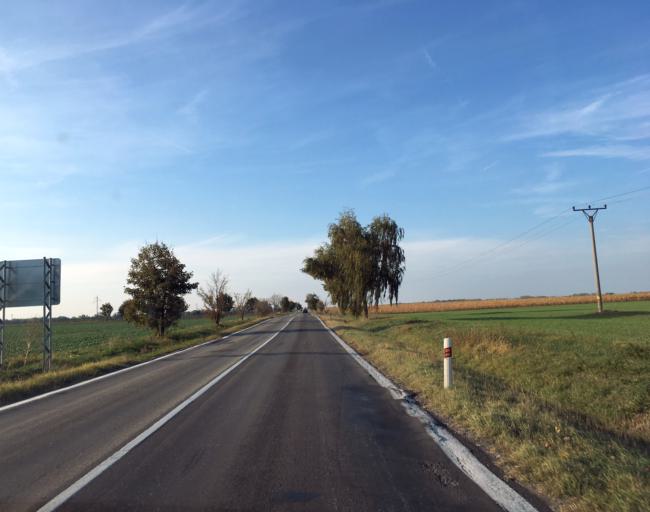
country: SK
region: Nitriansky
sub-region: Okres Nove Zamky
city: Nove Zamky
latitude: 48.0267
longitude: 18.1375
